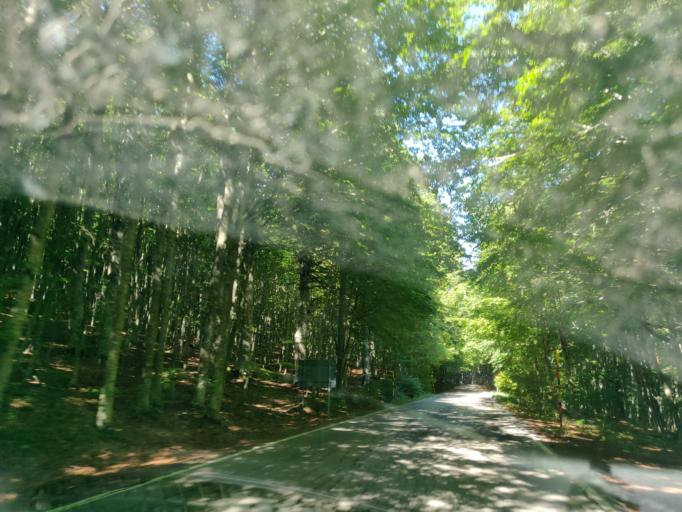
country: IT
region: Tuscany
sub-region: Provincia di Siena
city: Abbadia San Salvatore
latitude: 42.9025
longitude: 11.6243
